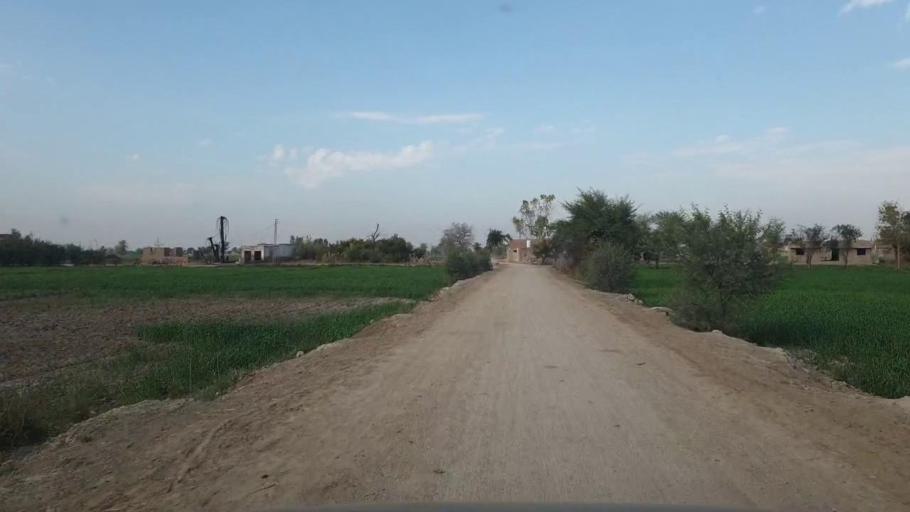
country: PK
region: Sindh
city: Sakrand
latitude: 26.0160
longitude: 68.4235
